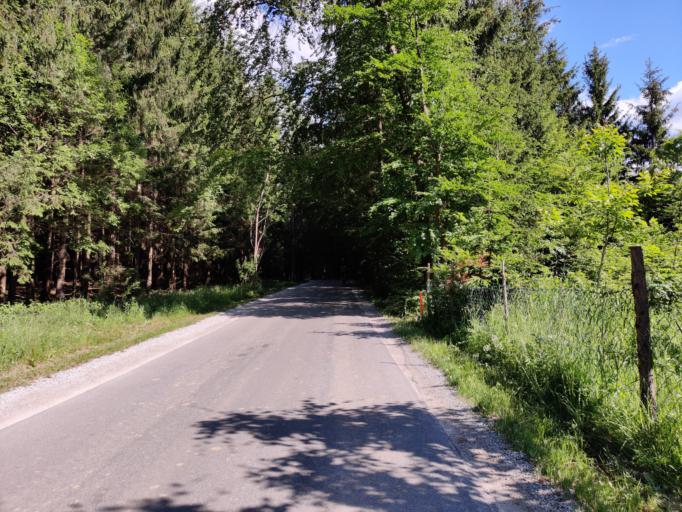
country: AT
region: Styria
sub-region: Politischer Bezirk Graz-Umgebung
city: Thal
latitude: 47.0421
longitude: 15.3653
